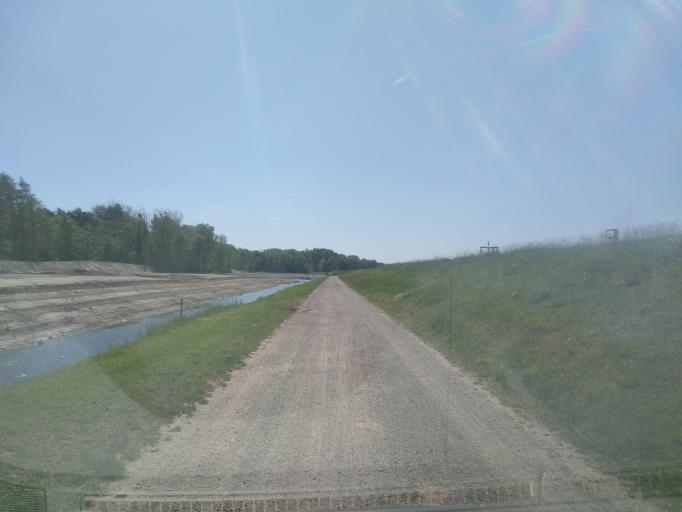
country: DE
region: Baden-Wuerttemberg
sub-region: Freiburg Region
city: Breisach am Rhein
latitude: 48.0607
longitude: 7.5749
